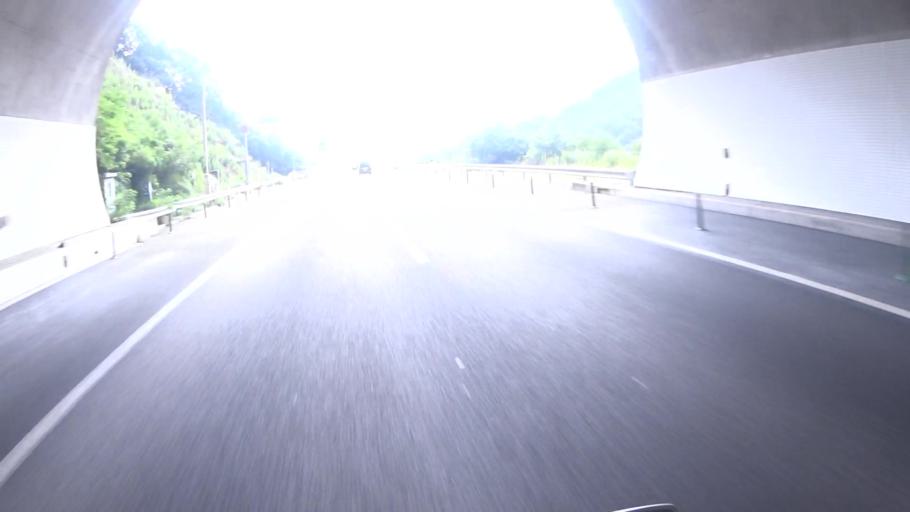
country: JP
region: Mie
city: Kameyama
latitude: 34.9158
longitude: 136.3807
